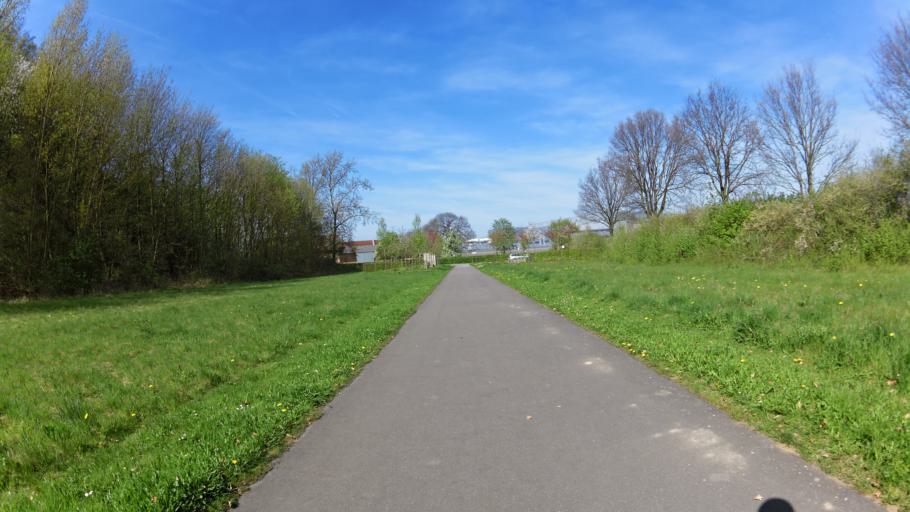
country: DE
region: North Rhine-Westphalia
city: Baesweiler
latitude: 50.9124
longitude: 6.1545
